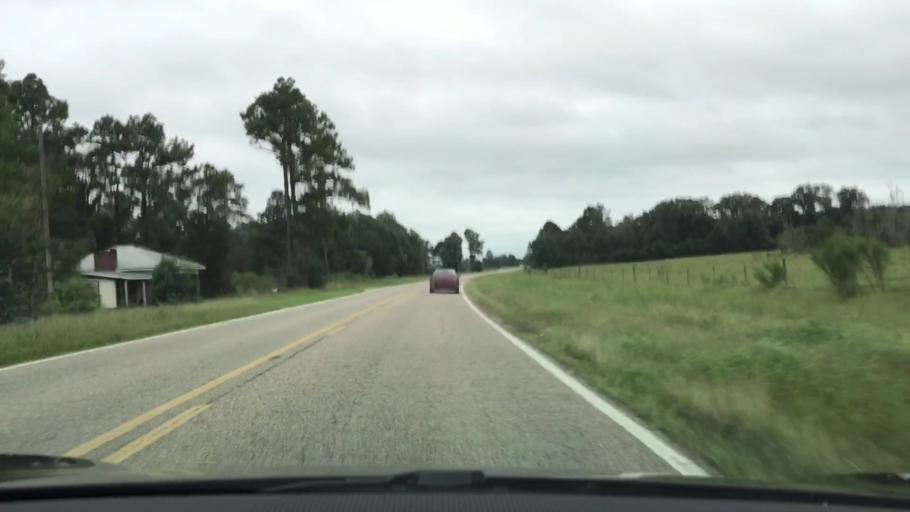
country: US
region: Alabama
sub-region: Geneva County
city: Samson
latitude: 31.1529
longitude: -86.1409
